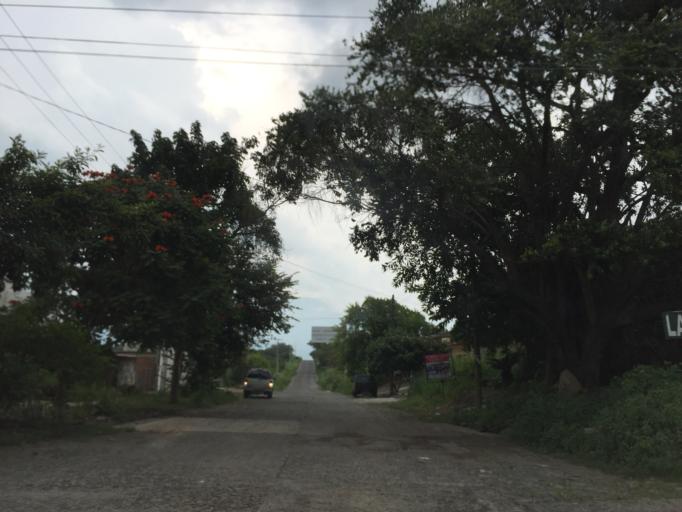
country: MX
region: Colima
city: Comala
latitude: 19.3319
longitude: -103.7646
